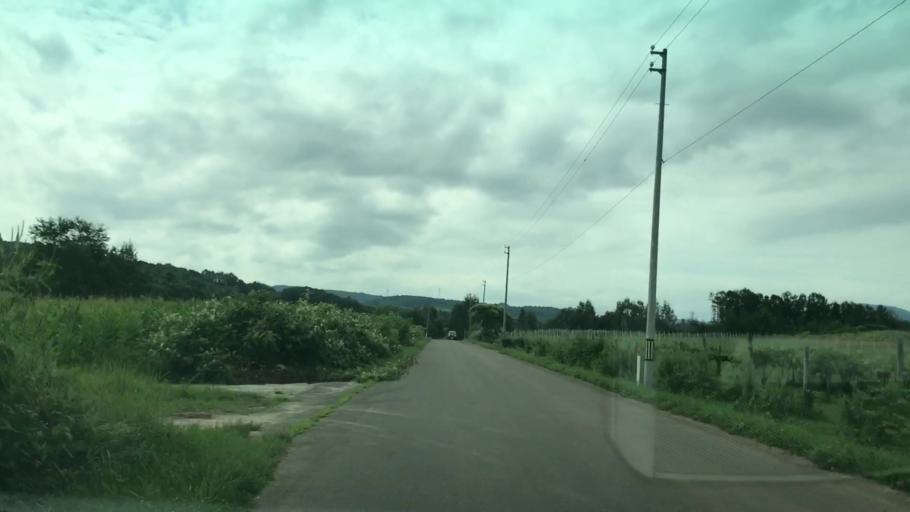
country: JP
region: Hokkaido
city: Yoichi
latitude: 43.1748
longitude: 140.8382
